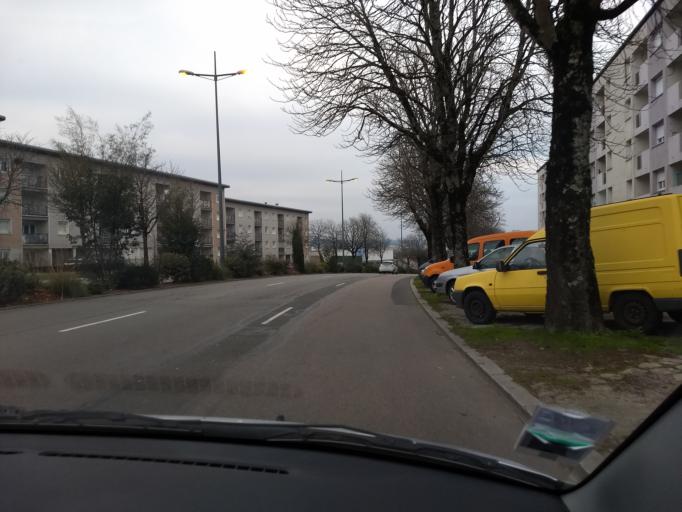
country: FR
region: Limousin
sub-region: Departement de la Haute-Vienne
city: Isle
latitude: 45.8253
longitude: 1.2258
